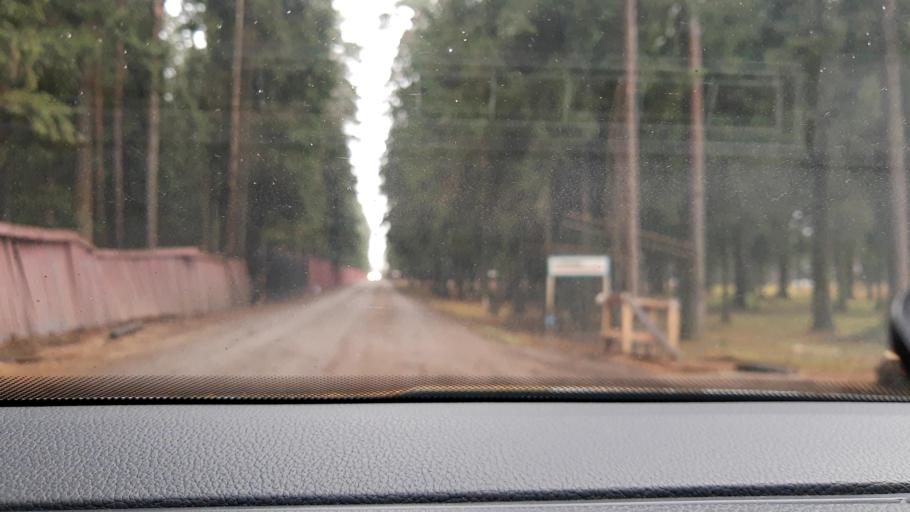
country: RU
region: Moskovskaya
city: Pushkino
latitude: 56.0099
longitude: 37.8894
